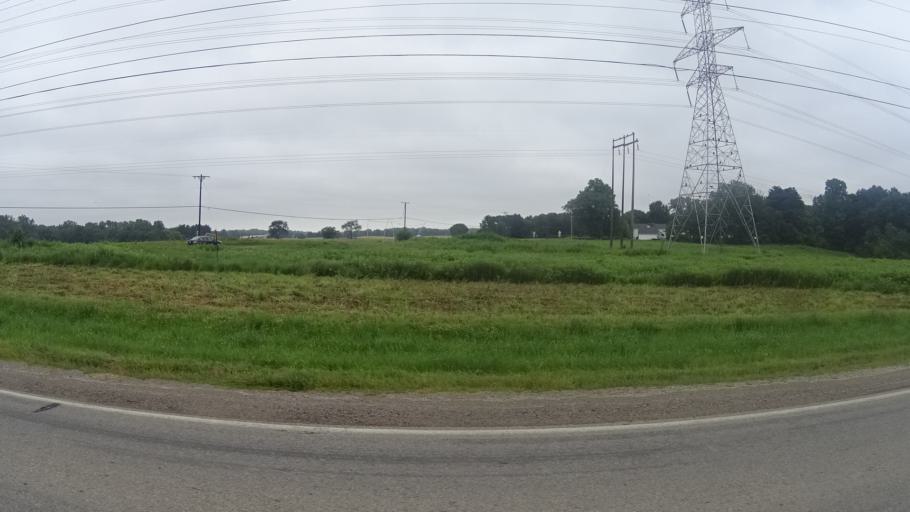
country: US
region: Ohio
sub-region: Erie County
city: Milan
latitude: 41.3365
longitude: -82.5862
